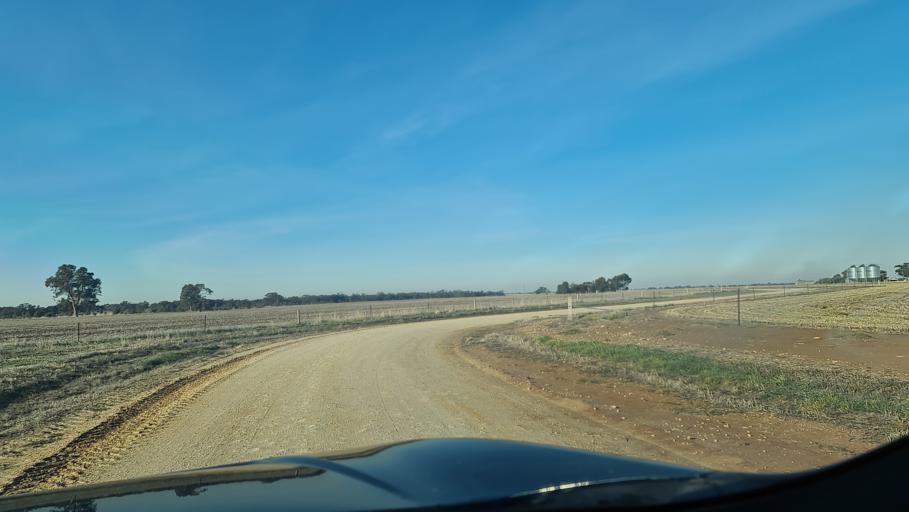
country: AU
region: Victoria
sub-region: Horsham
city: Horsham
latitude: -36.3607
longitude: 142.3966
